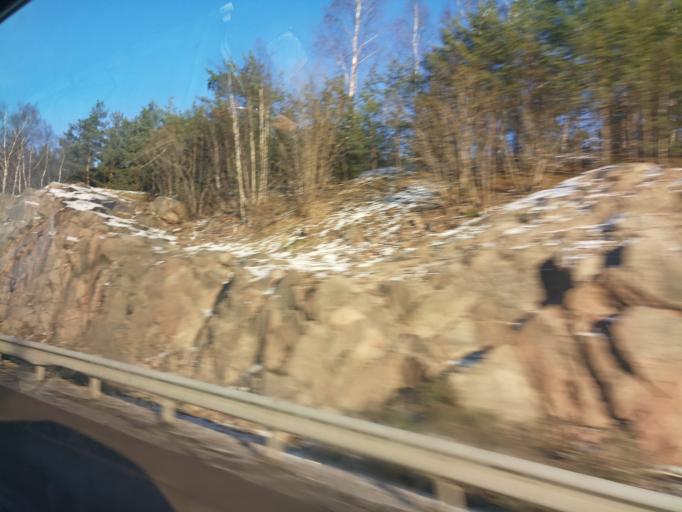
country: SE
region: Stockholm
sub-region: Upplands Vasby Kommun
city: Upplands Vaesby
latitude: 59.5504
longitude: 17.8997
